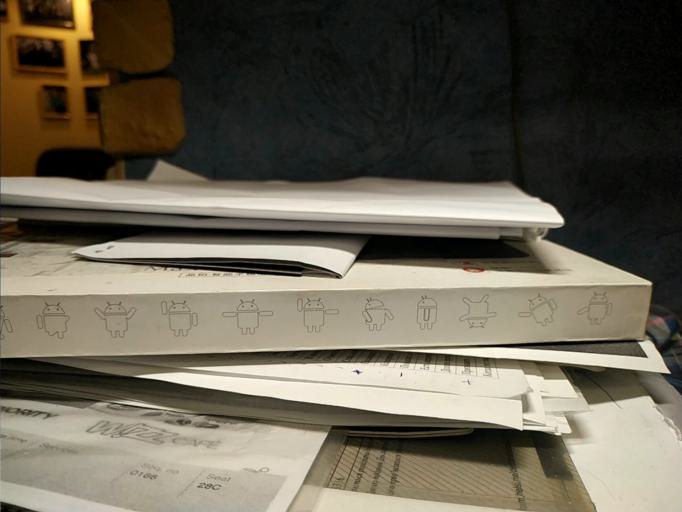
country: RU
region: Tverskaya
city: Zubtsov
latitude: 56.0808
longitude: 34.7993
